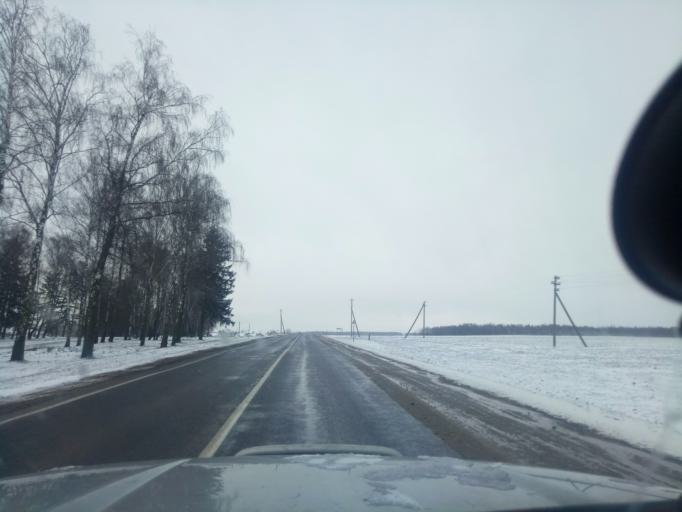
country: BY
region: Minsk
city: Kapyl'
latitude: 53.1097
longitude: 27.0582
